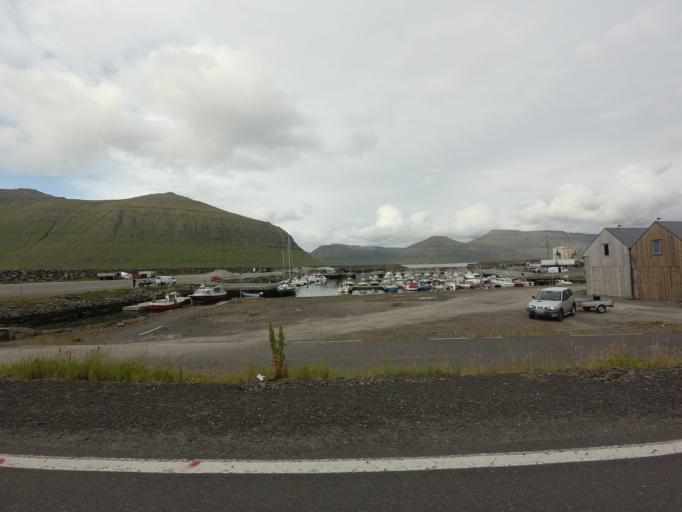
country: FO
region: Eysturoy
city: Eystur
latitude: 62.2126
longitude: -6.7108
